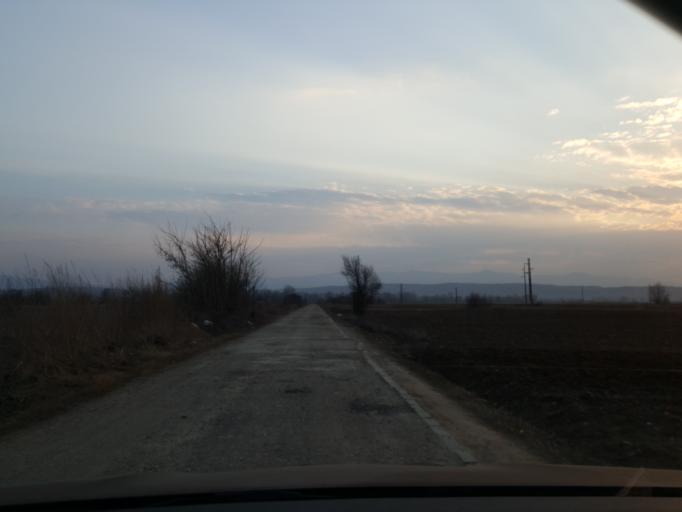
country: RS
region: Central Serbia
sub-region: Nisavski Okrug
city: Aleksinac
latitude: 43.5510
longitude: 21.6821
